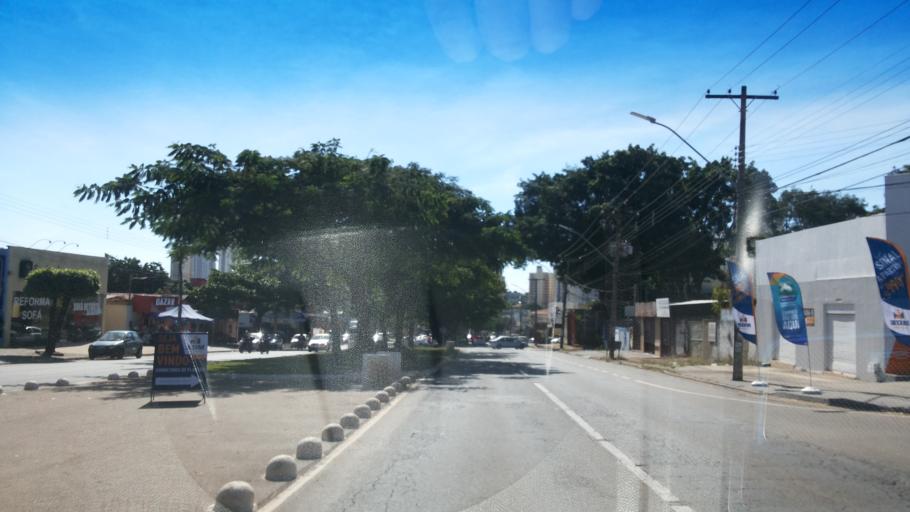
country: BR
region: Goias
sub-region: Goiania
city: Goiania
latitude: -16.7042
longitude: -49.2474
